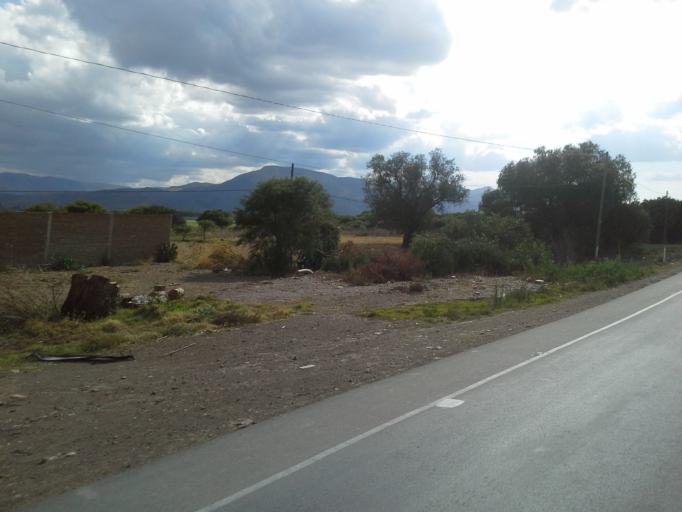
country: BO
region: Cochabamba
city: Tarata
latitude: -17.5443
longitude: -66.0169
